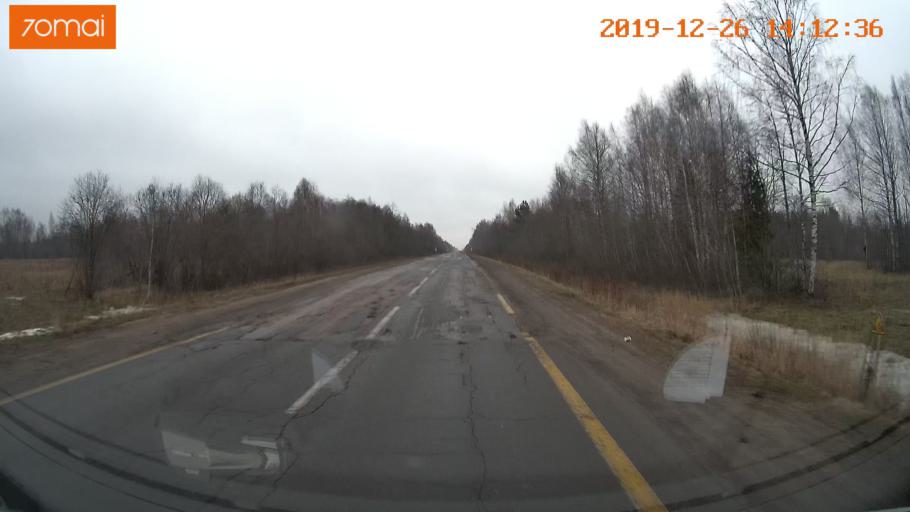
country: RU
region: Jaroslavl
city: Poshekhon'ye
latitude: 58.5113
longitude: 38.9932
